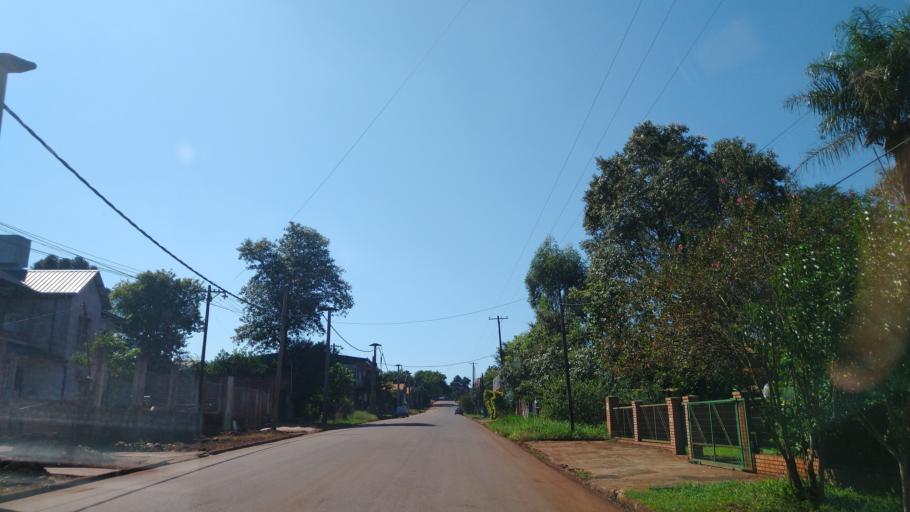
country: AR
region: Misiones
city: Puerto Libertad
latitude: -25.9769
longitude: -54.5756
